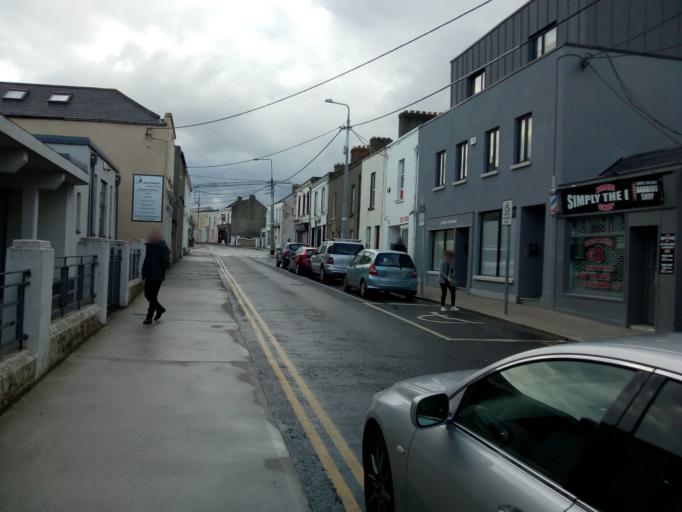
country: IE
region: Leinster
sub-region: Dun Laoghaire-Rathdown
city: Dun Laoghaire
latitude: 53.2915
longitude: -6.1372
